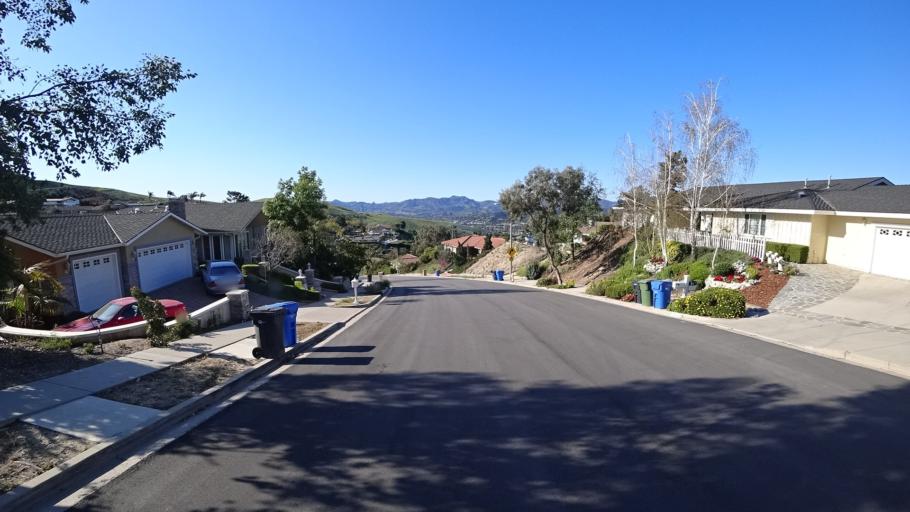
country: US
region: California
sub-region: Ventura County
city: Thousand Oaks
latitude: 34.1962
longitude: -118.8360
